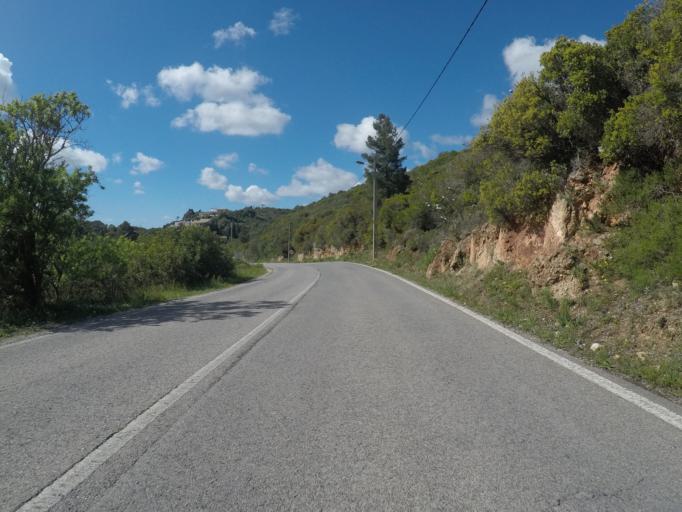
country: PT
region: Faro
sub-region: Vila do Bispo
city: Vila do Bispo
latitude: 37.0702
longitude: -8.8263
